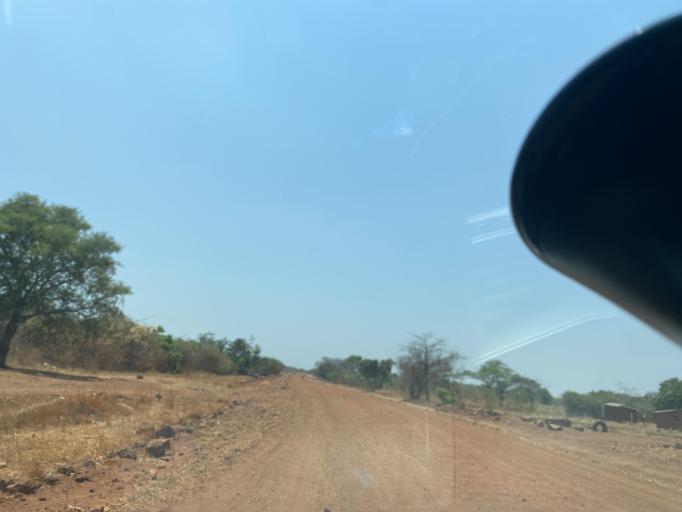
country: ZM
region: Lusaka
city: Lusaka
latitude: -15.4533
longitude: 27.9480
